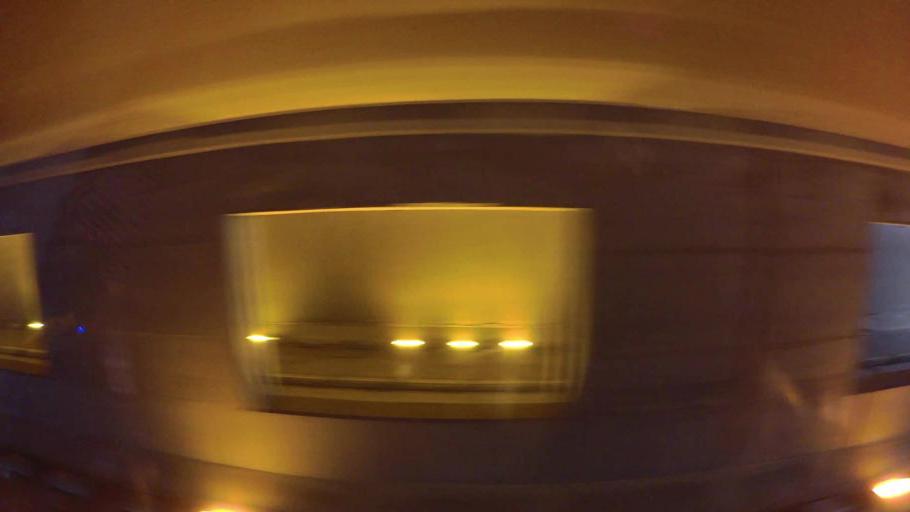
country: JO
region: Zarqa
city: Zarqa
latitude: 32.0608
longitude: 36.0942
